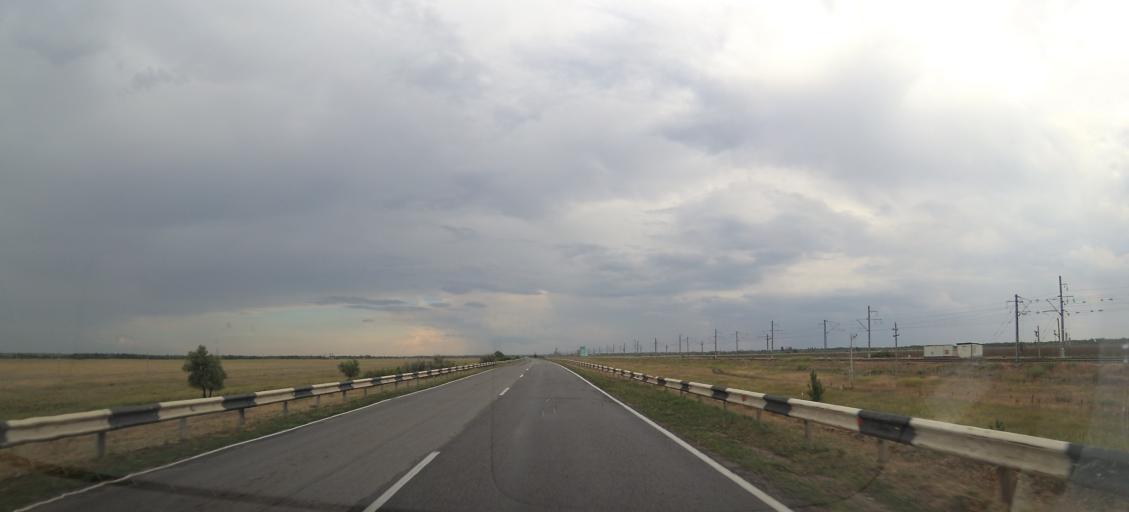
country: RU
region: Rostov
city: Dubovskoye
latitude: 47.3886
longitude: 42.7132
